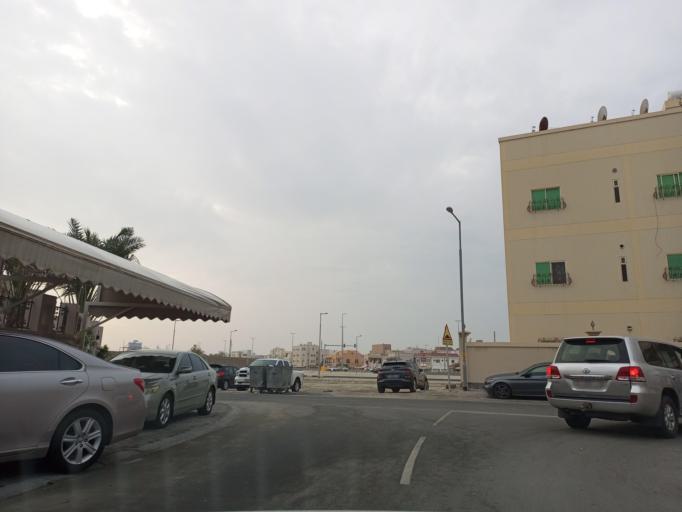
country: BH
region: Muharraq
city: Al Hadd
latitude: 26.2465
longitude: 50.6420
